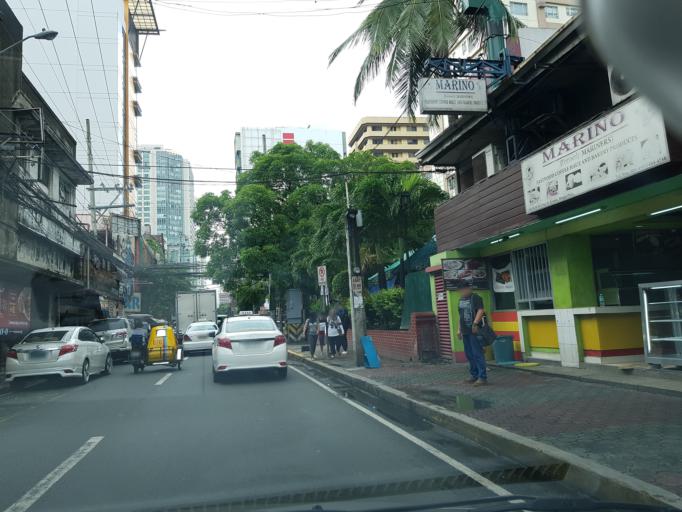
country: PH
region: Metro Manila
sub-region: City of Manila
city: Port Area
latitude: 14.5762
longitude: 120.9809
